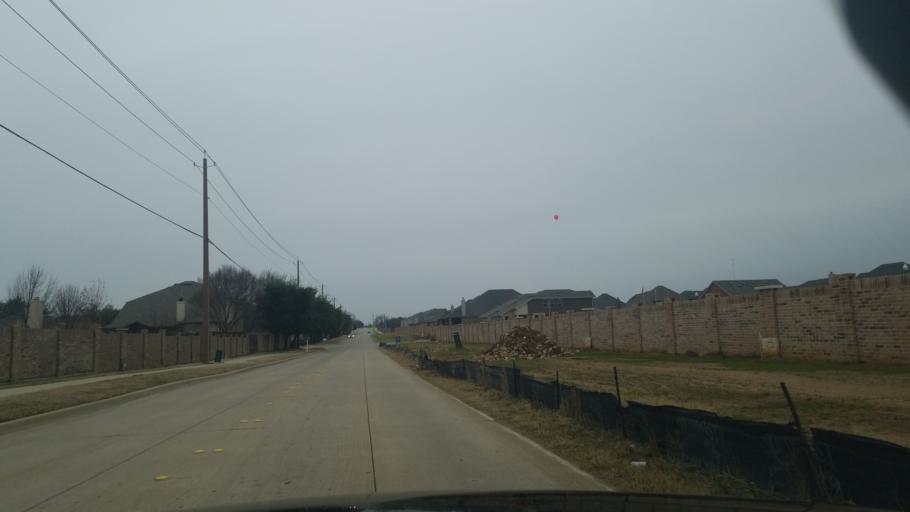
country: US
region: Texas
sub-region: Denton County
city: Corinth
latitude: 33.1708
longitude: -97.0718
